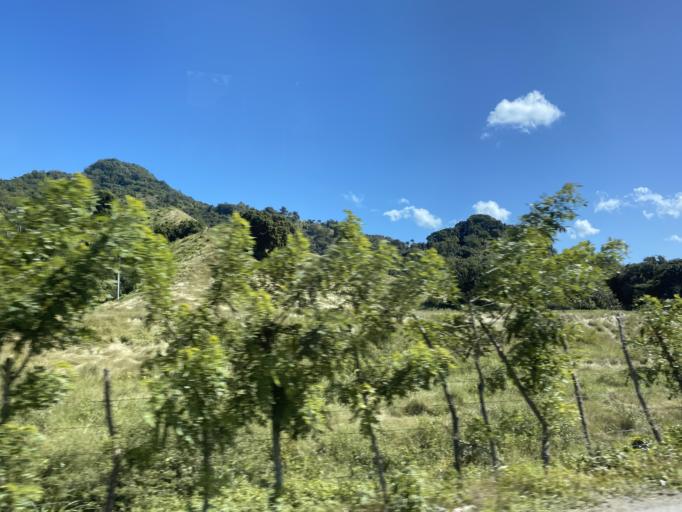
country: DO
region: Puerto Plata
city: Imbert
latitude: 19.8126
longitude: -70.7792
